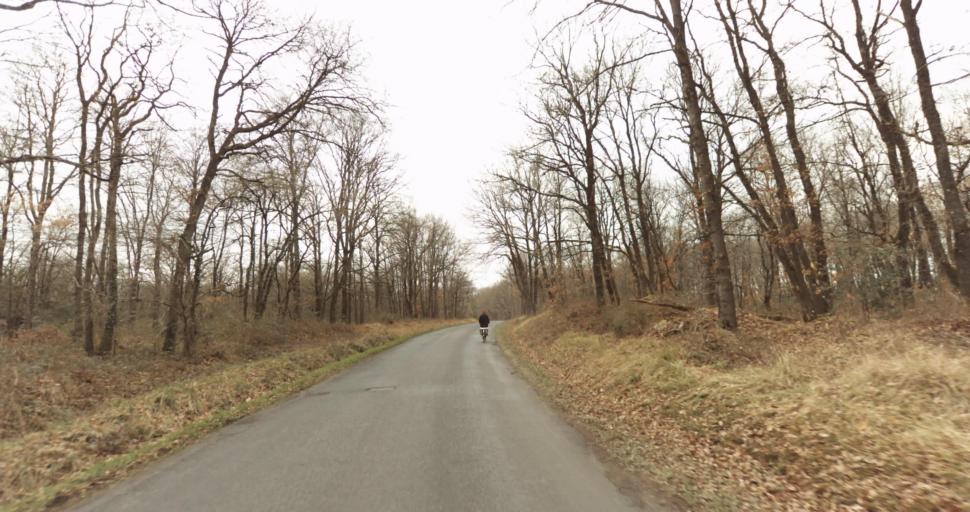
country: FR
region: Pays de la Loire
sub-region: Departement de Maine-et-Loire
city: Distre
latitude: 47.2537
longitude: -0.1184
